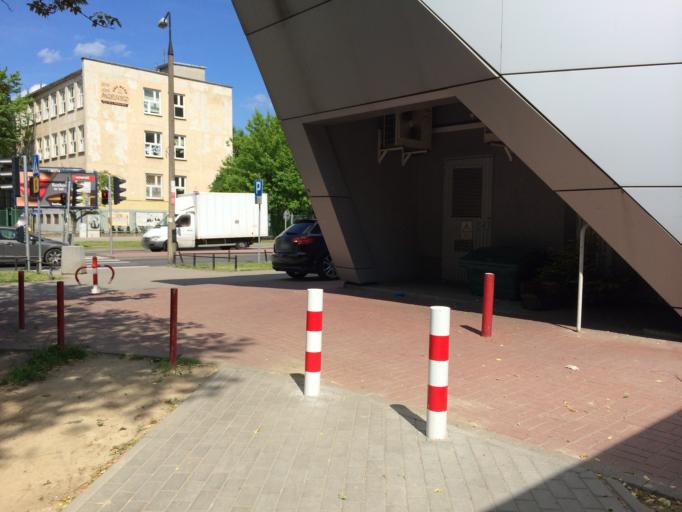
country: PL
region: Masovian Voivodeship
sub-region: Warszawa
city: Praga Poludnie
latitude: 52.2369
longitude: 21.1040
